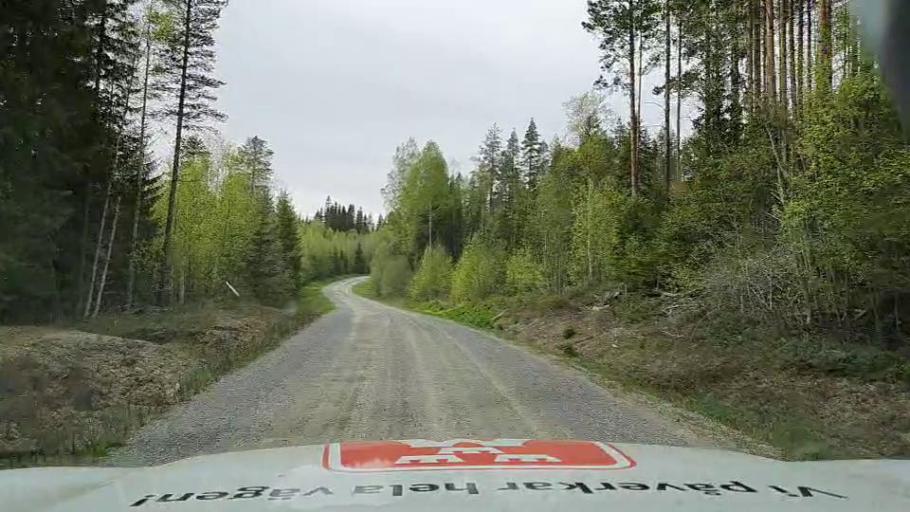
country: SE
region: Jaemtland
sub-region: Bergs Kommun
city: Hoverberg
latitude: 62.5322
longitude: 14.9120
